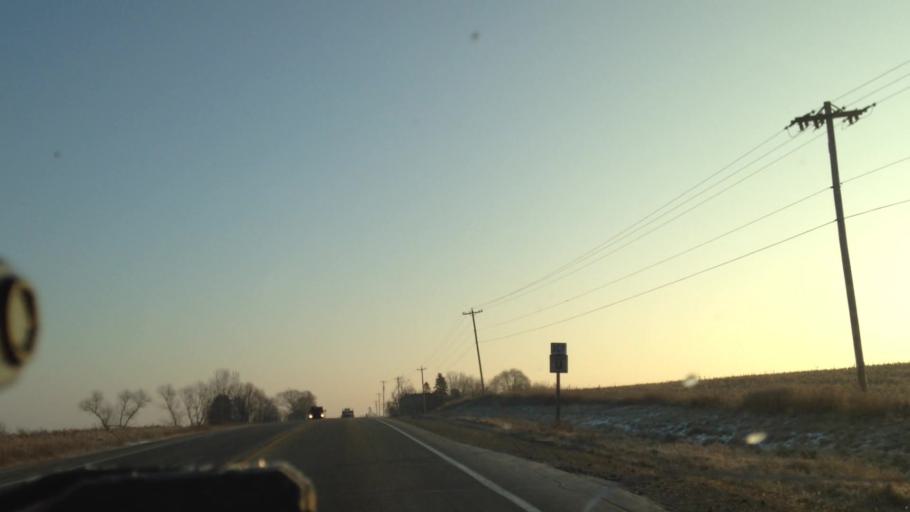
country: US
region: Wisconsin
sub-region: Washington County
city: Hartford
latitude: 43.4223
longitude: -88.4013
